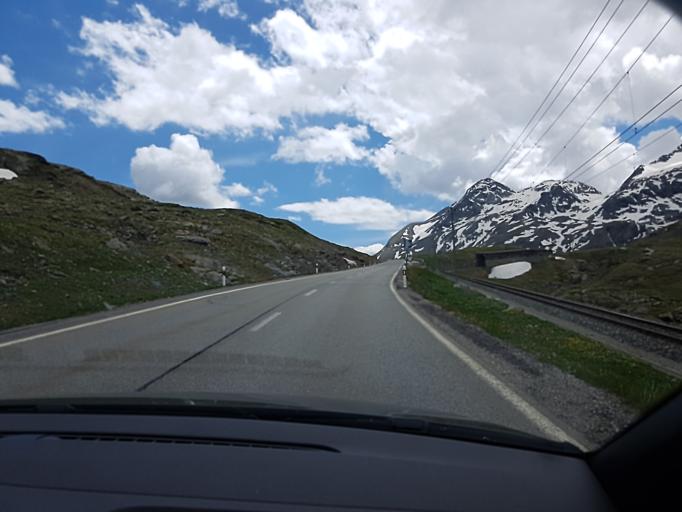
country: CH
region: Grisons
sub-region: Bernina District
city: Poschiavo
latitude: 46.4230
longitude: 10.0019
